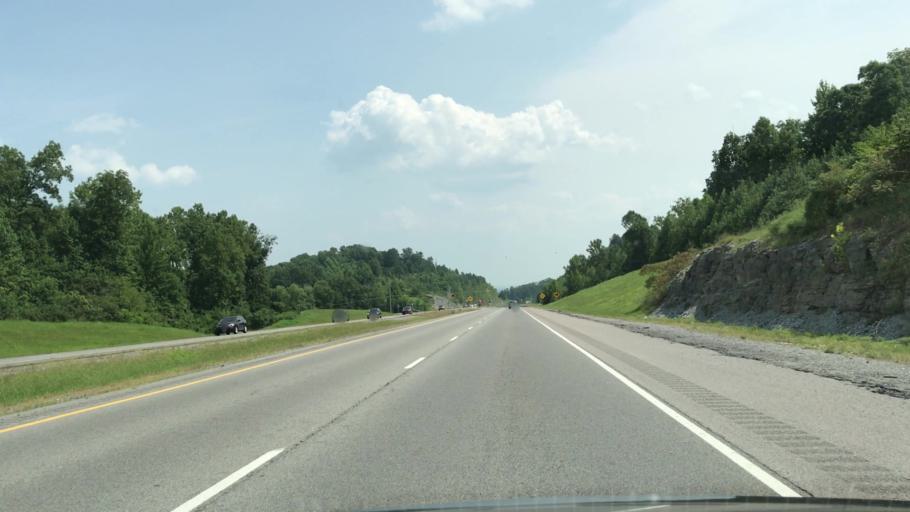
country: US
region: Tennessee
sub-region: Sumner County
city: Gallatin
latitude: 36.4742
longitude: -86.4749
